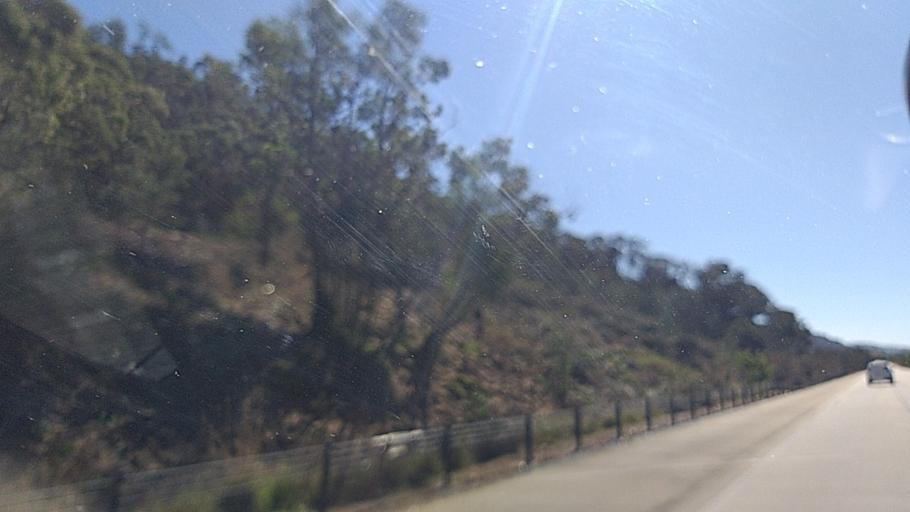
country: AU
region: New South Wales
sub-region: Yass Valley
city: Gundaroo
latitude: -35.0226
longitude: 149.3782
